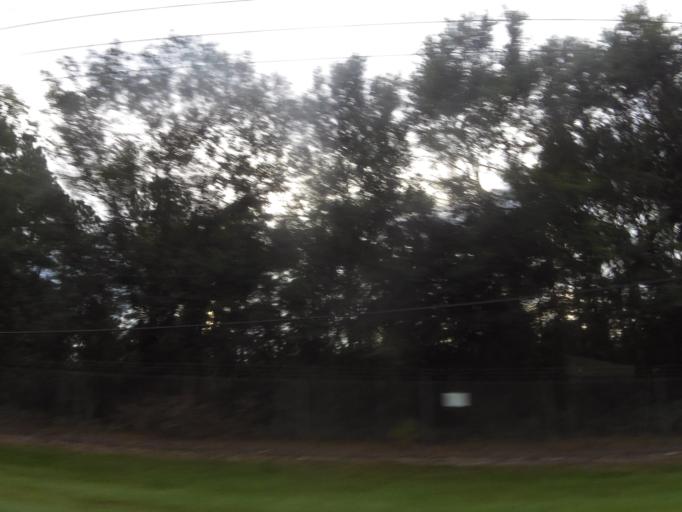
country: US
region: Florida
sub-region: Clay County
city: Bellair-Meadowbrook Terrace
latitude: 30.2842
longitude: -81.7973
